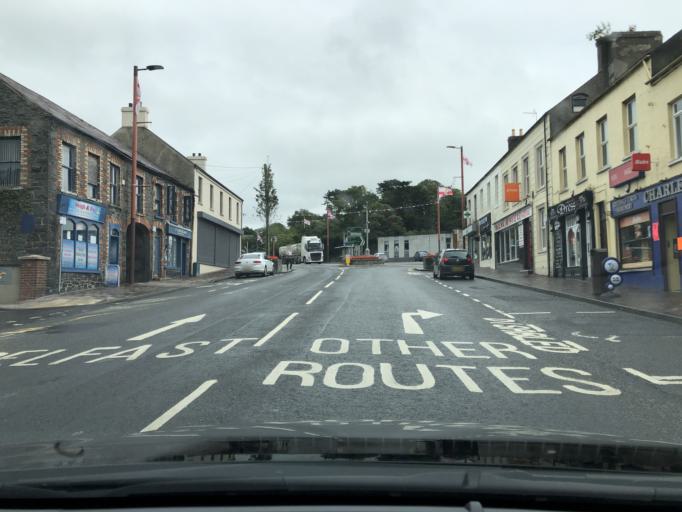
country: GB
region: Northern Ireland
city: Ballynahinch
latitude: 54.4035
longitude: -5.8953
